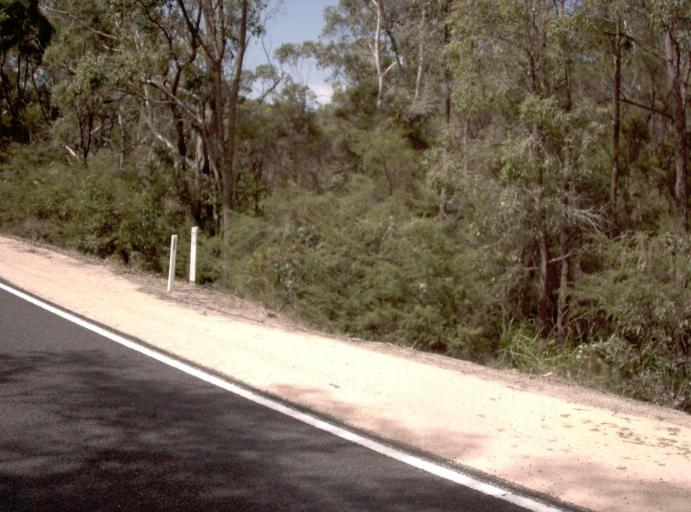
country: AU
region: New South Wales
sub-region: Bega Valley
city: Eden
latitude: -37.4323
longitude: 149.6449
